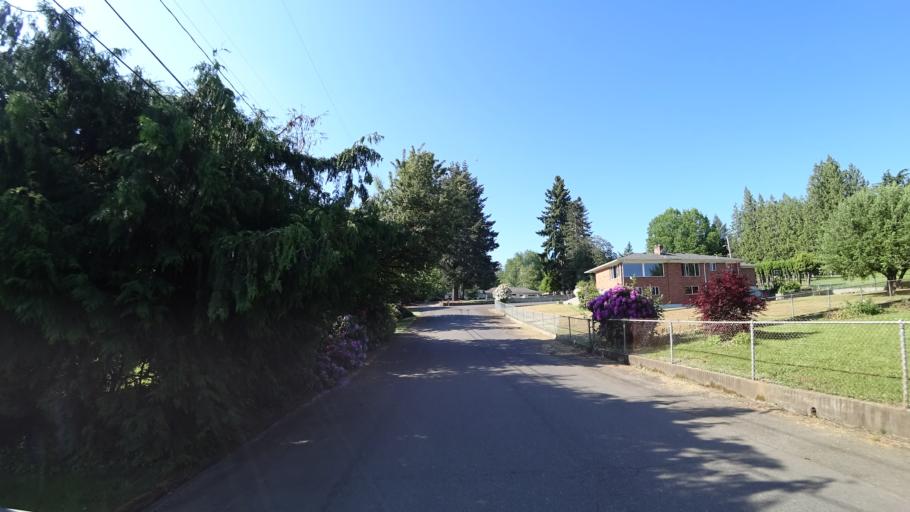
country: US
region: Oregon
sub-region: Clackamas County
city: Happy Valley
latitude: 45.4710
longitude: -122.5326
